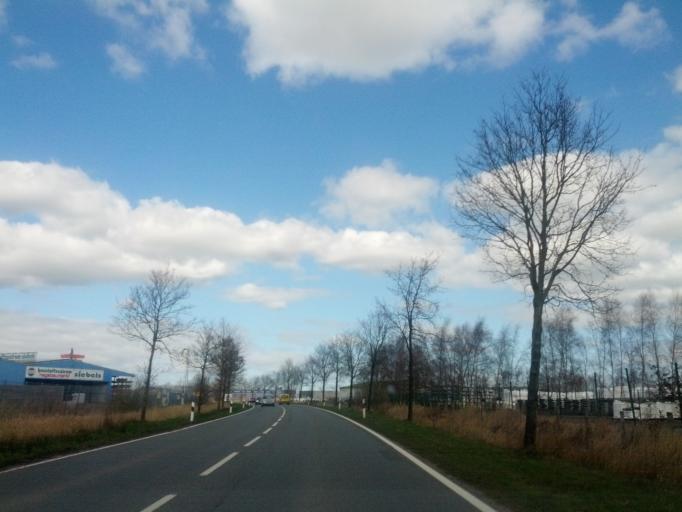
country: DE
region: Lower Saxony
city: Wittmund
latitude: 53.5801
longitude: 7.8006
